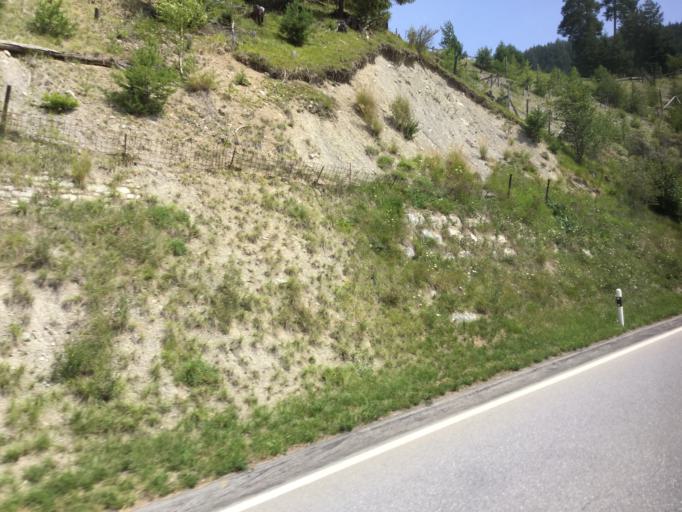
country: CH
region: Grisons
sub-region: Albula District
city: Tiefencastel
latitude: 46.6500
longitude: 9.5772
